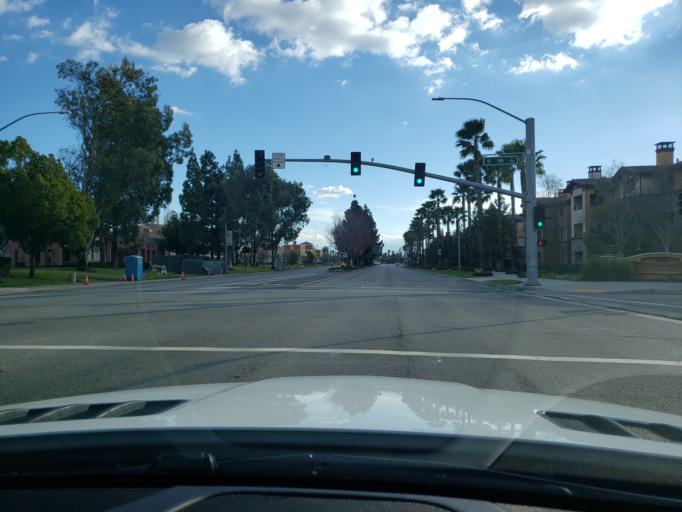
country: US
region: California
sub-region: San Bernardino County
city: Rancho Cucamonga
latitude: 34.0811
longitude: -117.5584
